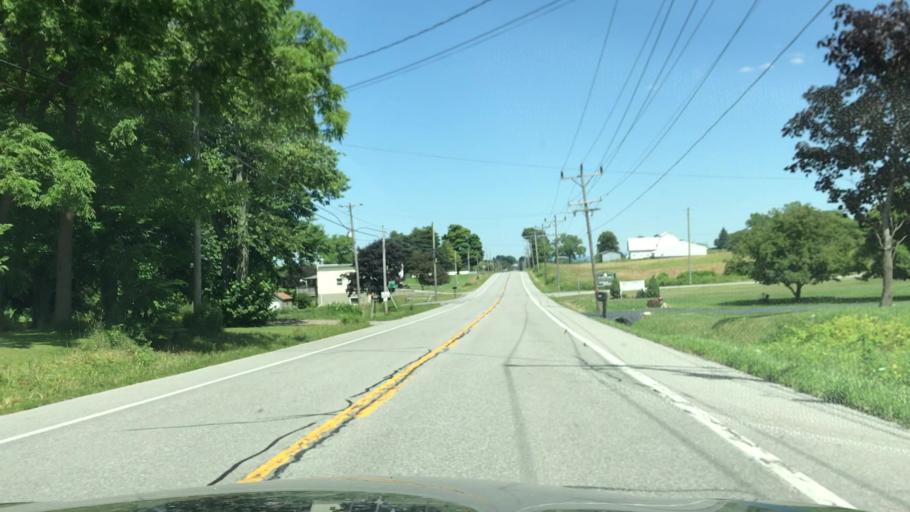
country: US
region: New York
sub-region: Wyoming County
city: Perry
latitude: 42.7448
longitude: -78.0516
